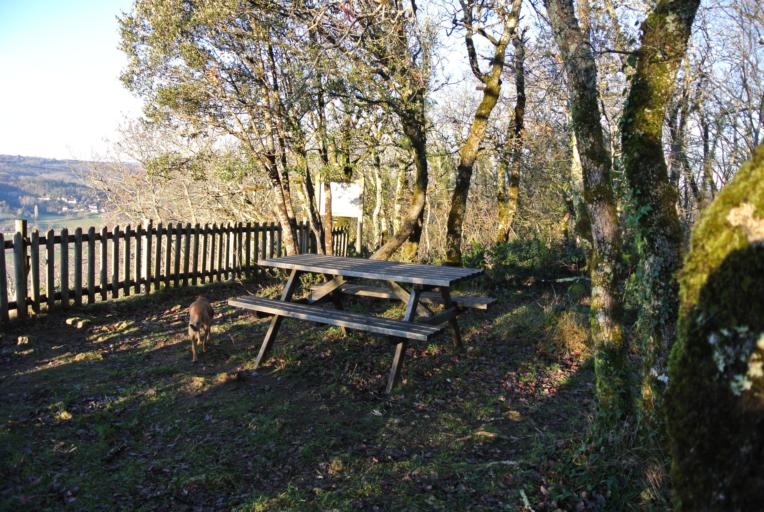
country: FR
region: Aquitaine
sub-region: Departement de la Dordogne
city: Le Bugue
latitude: 44.9119
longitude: 0.9746
